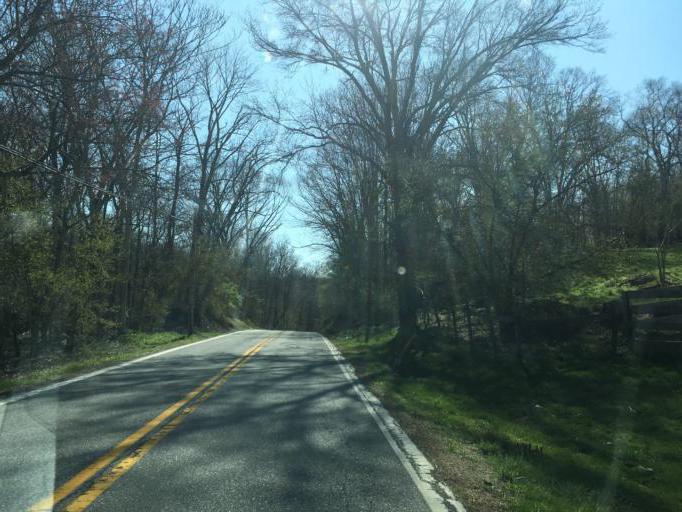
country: US
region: Maryland
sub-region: Frederick County
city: Myersville
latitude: 39.5730
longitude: -77.5428
